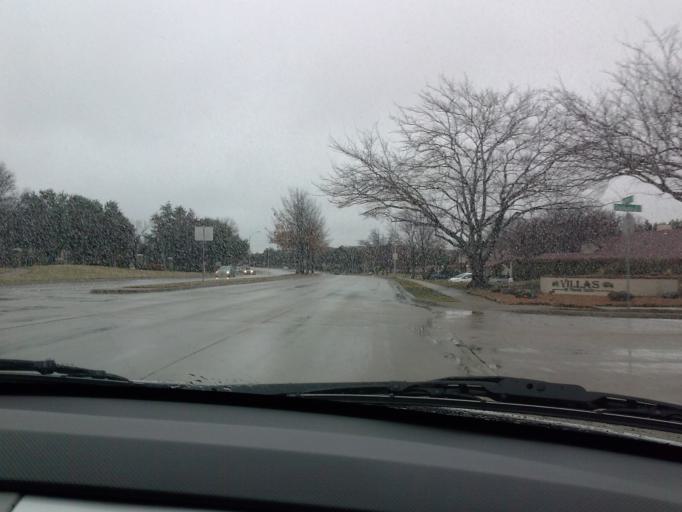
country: US
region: Texas
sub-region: Collin County
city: Allen
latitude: 33.0691
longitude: -96.7037
